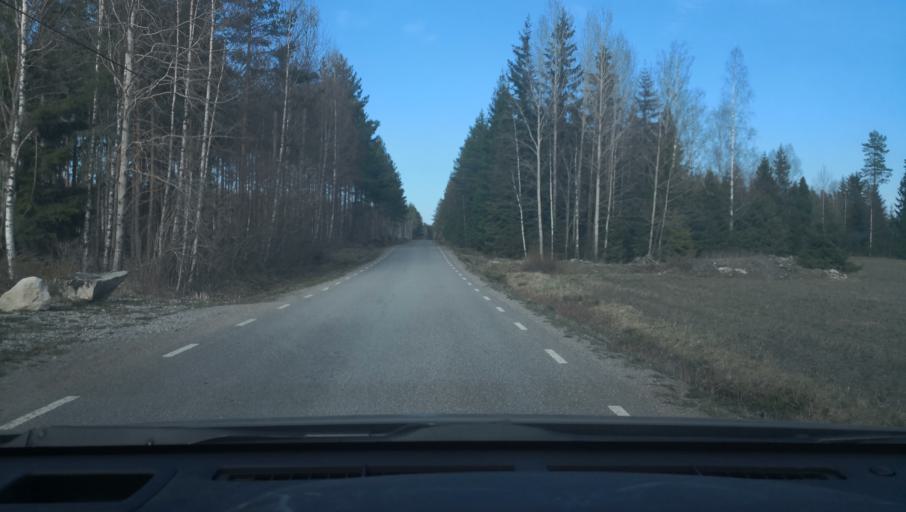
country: SE
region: Uppsala
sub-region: Heby Kommun
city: Heby
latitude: 59.9168
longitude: 16.8375
